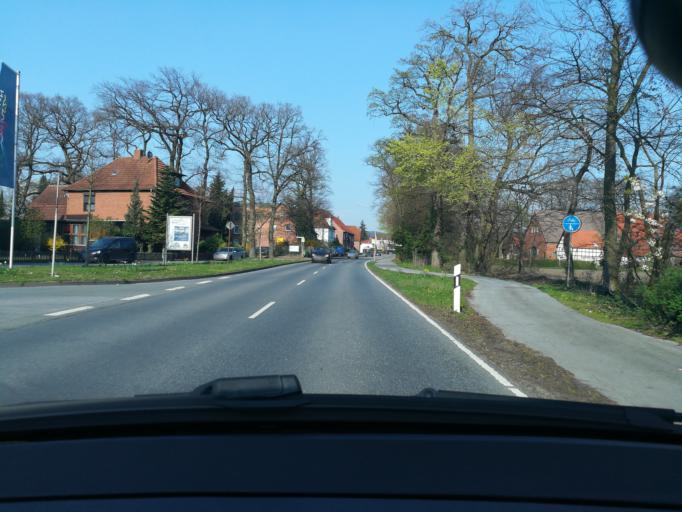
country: DE
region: North Rhine-Westphalia
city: Halle
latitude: 52.0498
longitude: 8.3504
